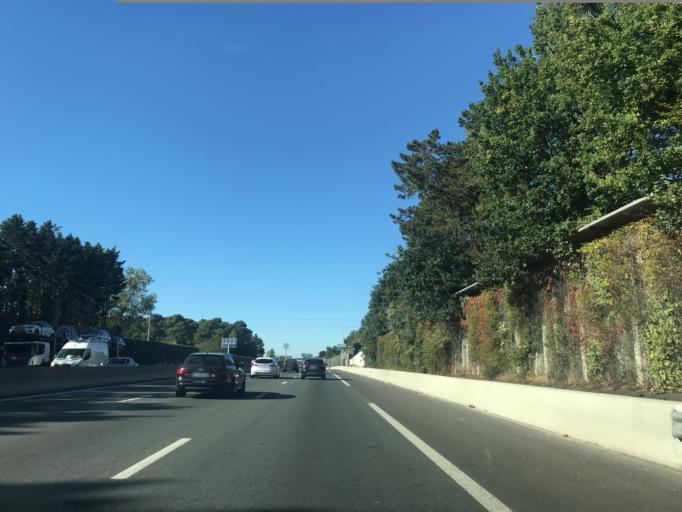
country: FR
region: Aquitaine
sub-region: Departement de la Gironde
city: Pessac
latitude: 44.7954
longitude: -0.6509
